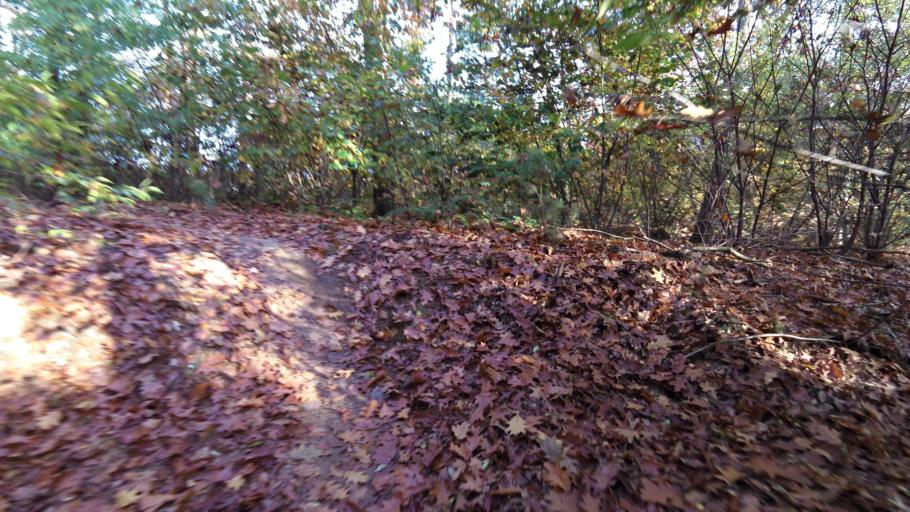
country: NL
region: Gelderland
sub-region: Gemeente Ede
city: Ede
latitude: 52.0677
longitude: 5.6621
